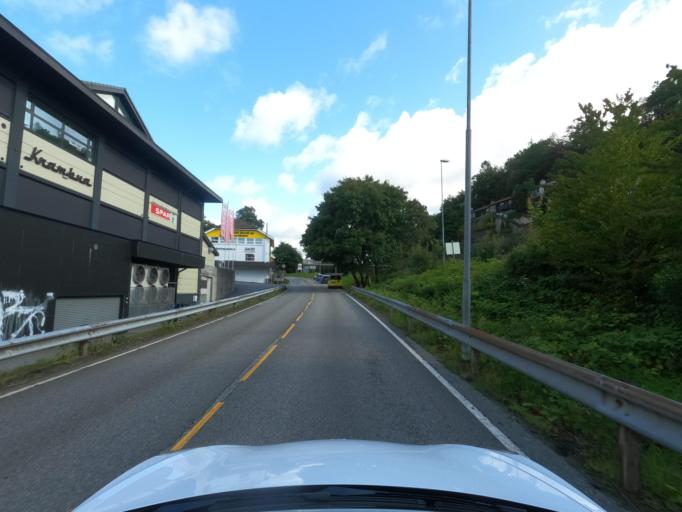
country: NO
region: Hordaland
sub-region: Bergen
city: Bergen
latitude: 60.3486
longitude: 5.3364
